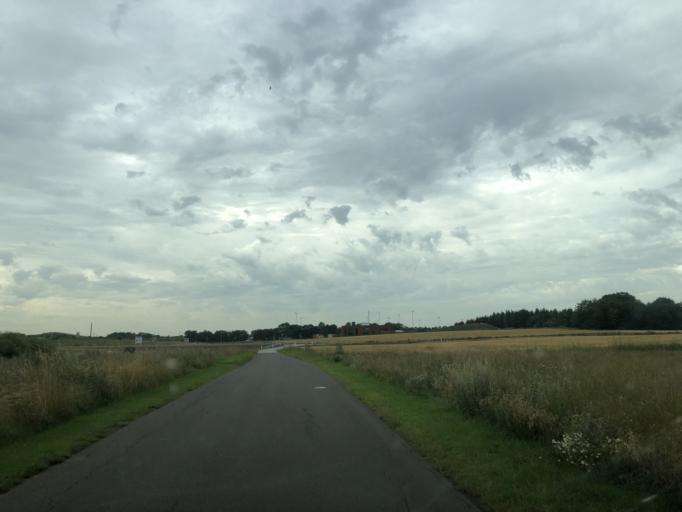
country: DK
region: Central Jutland
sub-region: Holstebro Kommune
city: Holstebro
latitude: 56.3951
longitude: 8.5819
